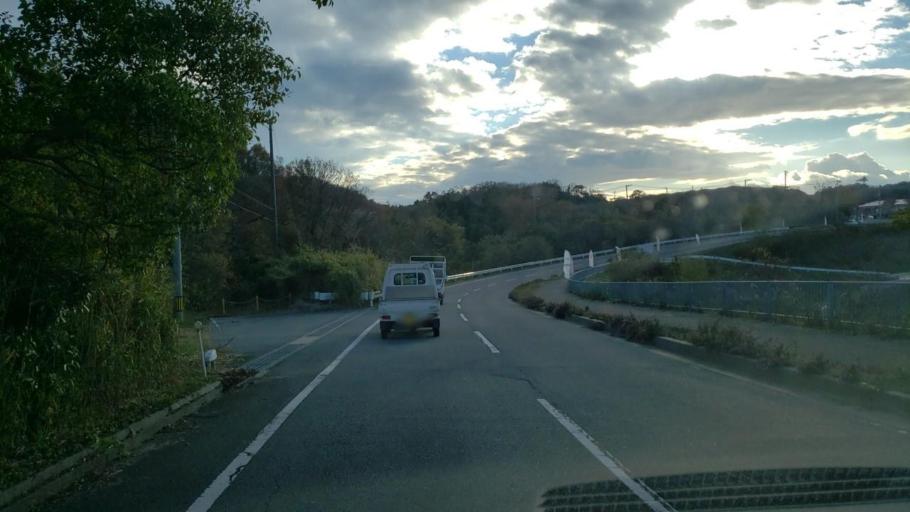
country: JP
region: Hyogo
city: Akashi
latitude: 34.5729
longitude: 134.9793
